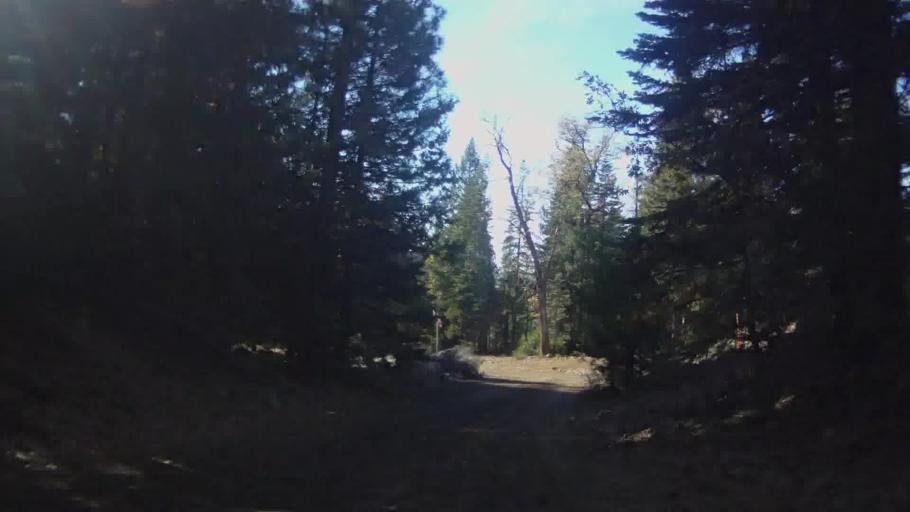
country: US
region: California
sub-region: Shasta County
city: Shingletown
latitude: 40.6603
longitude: -121.7938
